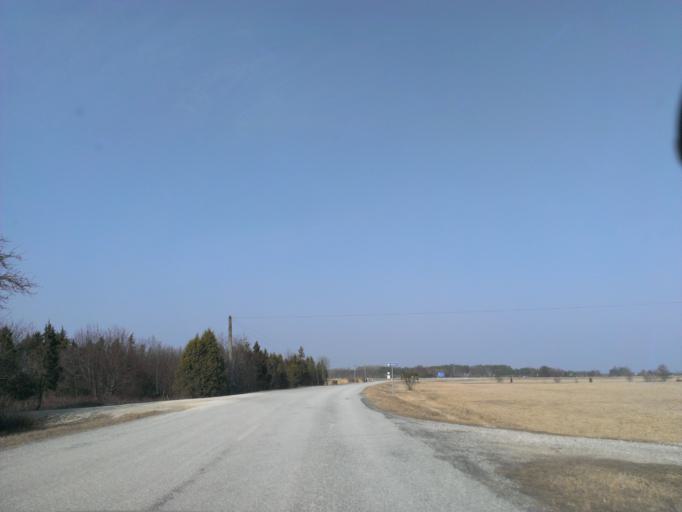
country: EE
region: Saare
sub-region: Orissaare vald
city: Orissaare
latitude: 58.5336
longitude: 23.1086
